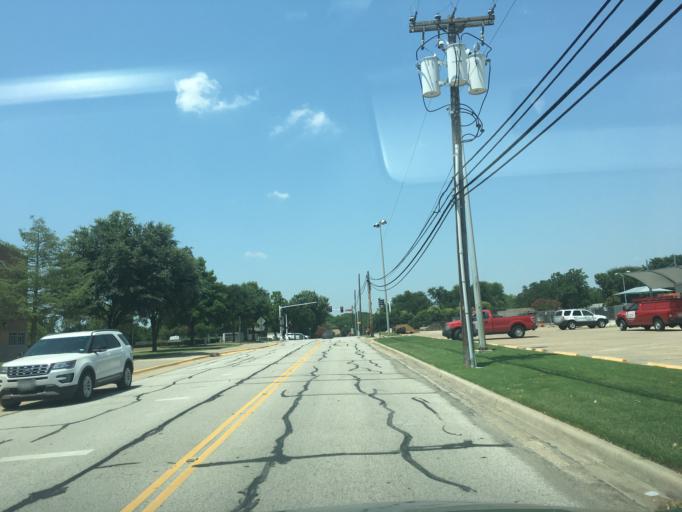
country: US
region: Texas
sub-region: Dallas County
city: Carrollton
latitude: 32.9379
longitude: -96.8802
